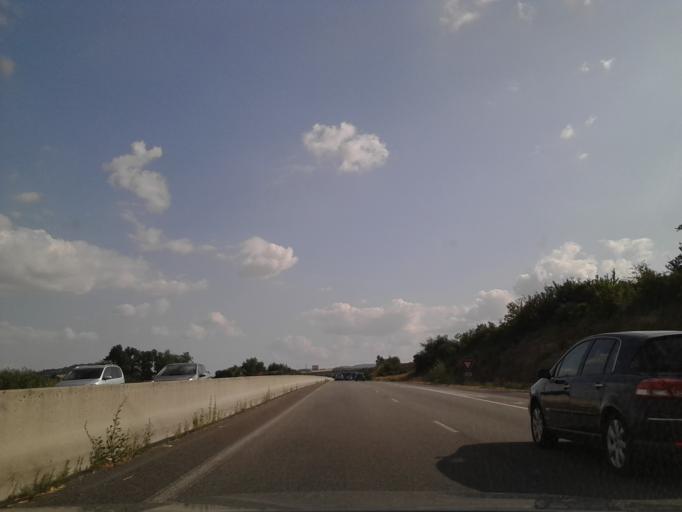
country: FR
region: Auvergne
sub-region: Departement du Puy-de-Dome
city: Perignat-les-Sarlieve
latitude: 45.7210
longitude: 3.1541
